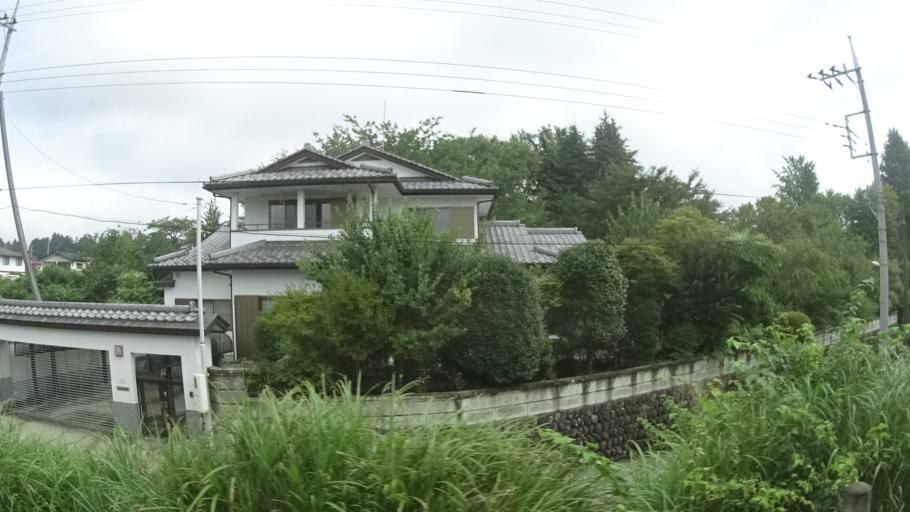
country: JP
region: Tochigi
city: Imaichi
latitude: 36.7244
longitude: 139.6788
